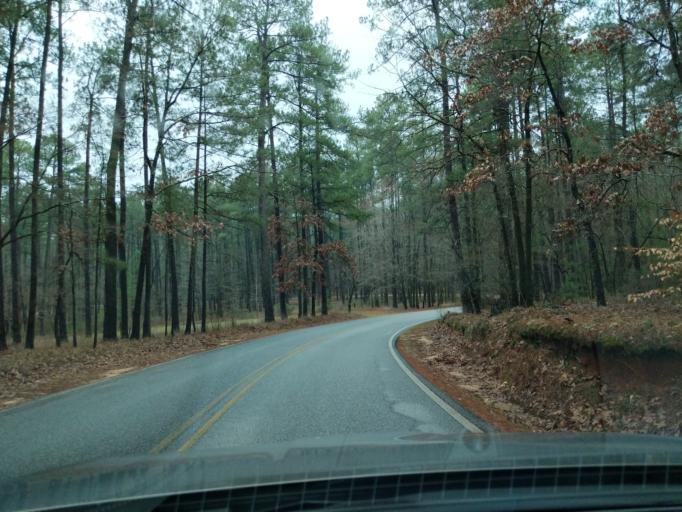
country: US
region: Georgia
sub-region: Columbia County
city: Appling
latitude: 33.6459
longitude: -82.3870
